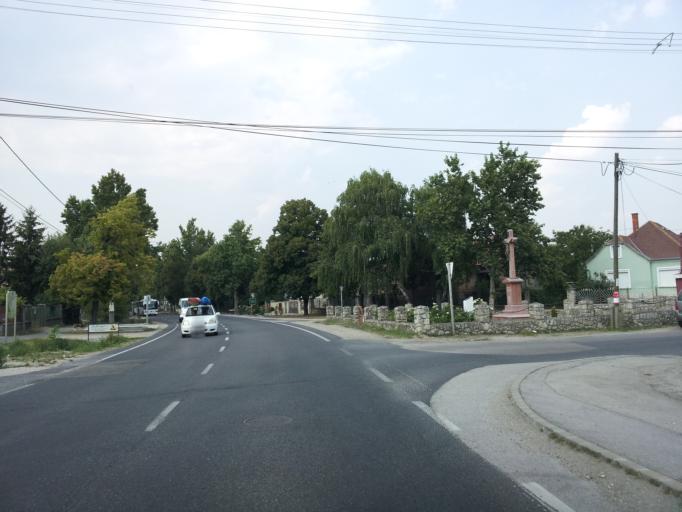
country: HU
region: Gyor-Moson-Sopron
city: Nyul
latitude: 47.5865
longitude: 17.6940
